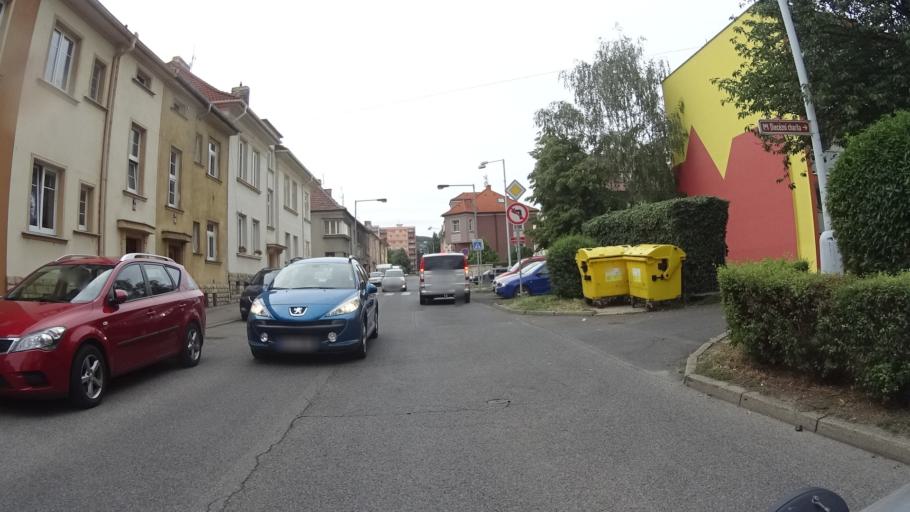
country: CZ
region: Ustecky
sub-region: Okres Litomerice
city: Litomerice
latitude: 50.5375
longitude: 14.1229
